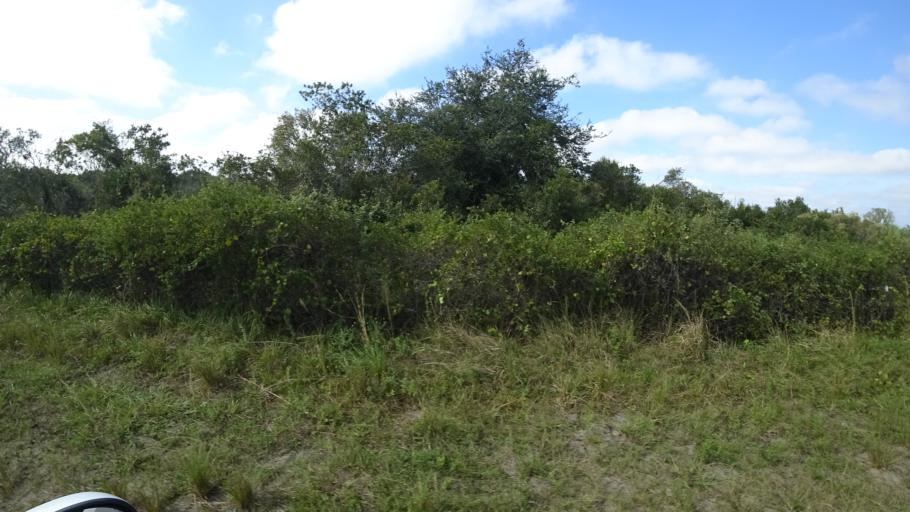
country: US
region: Florida
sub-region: DeSoto County
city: Arcadia
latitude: 27.2956
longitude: -82.0726
